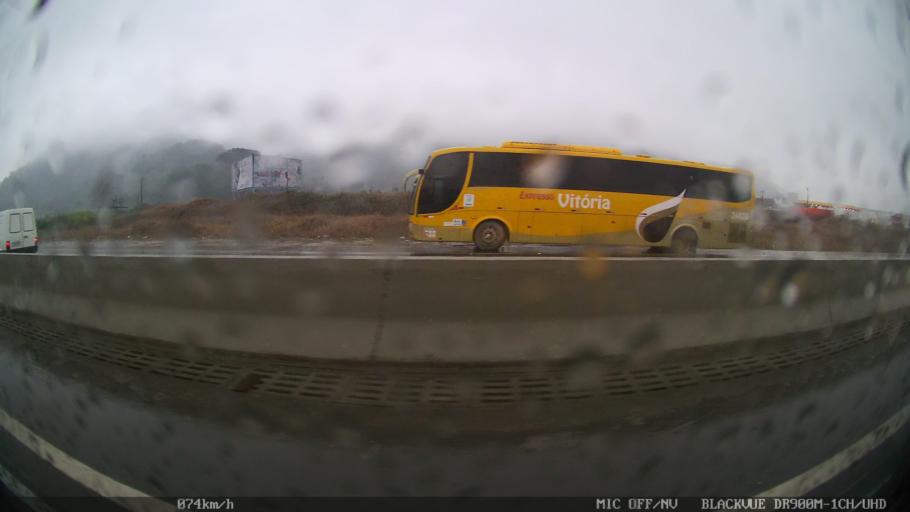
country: BR
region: Santa Catarina
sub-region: Navegantes
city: Navegantes
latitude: -26.8509
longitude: -48.7109
